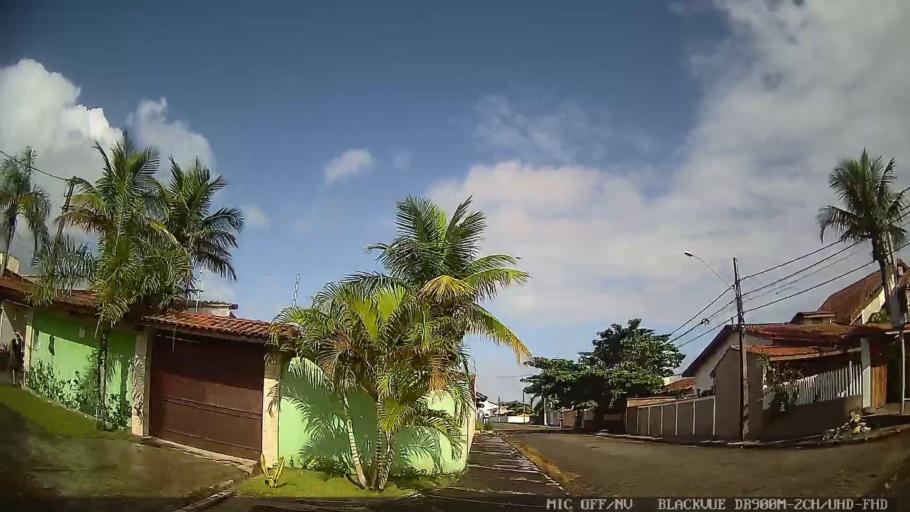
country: BR
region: Sao Paulo
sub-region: Itanhaem
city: Itanhaem
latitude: -24.2076
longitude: -46.8348
